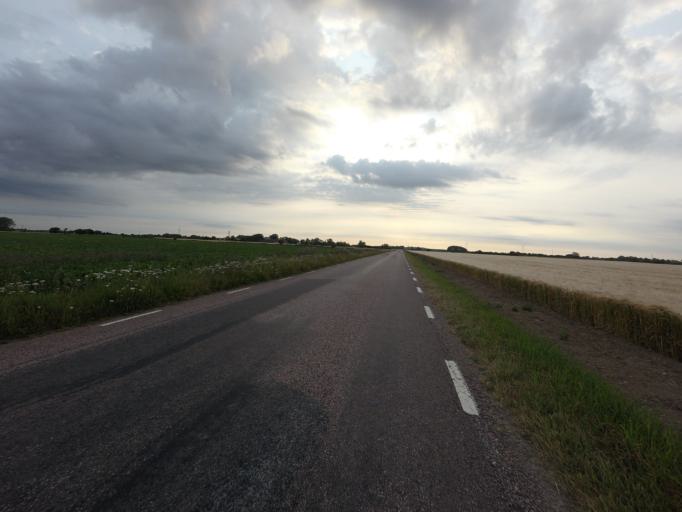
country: SE
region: Skane
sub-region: Hoganas Kommun
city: Hoganas
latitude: 56.1487
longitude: 12.6110
